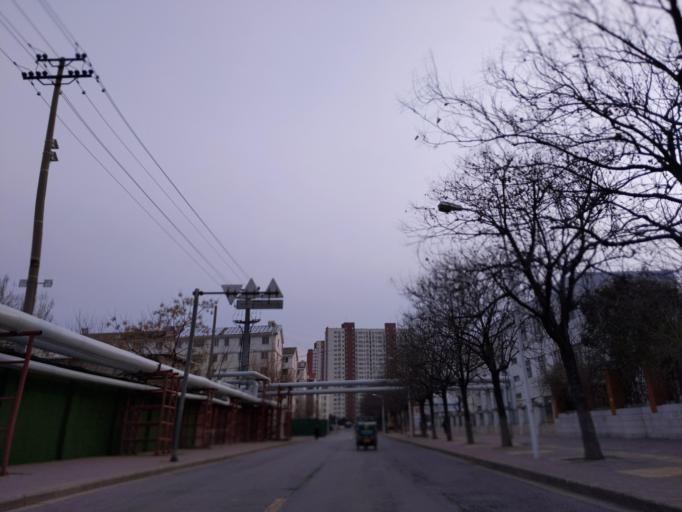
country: CN
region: Henan Sheng
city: Puyang
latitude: 35.7537
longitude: 115.0388
